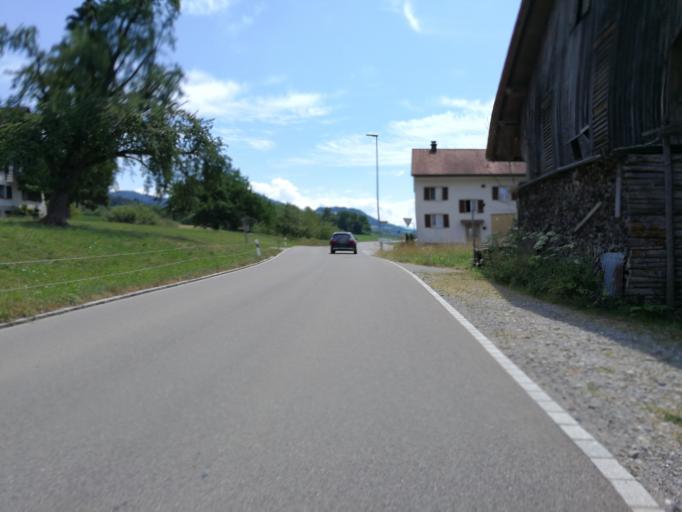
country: CH
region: Zurich
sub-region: Bezirk Hinwil
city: Hinwil
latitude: 47.3110
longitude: 8.8257
